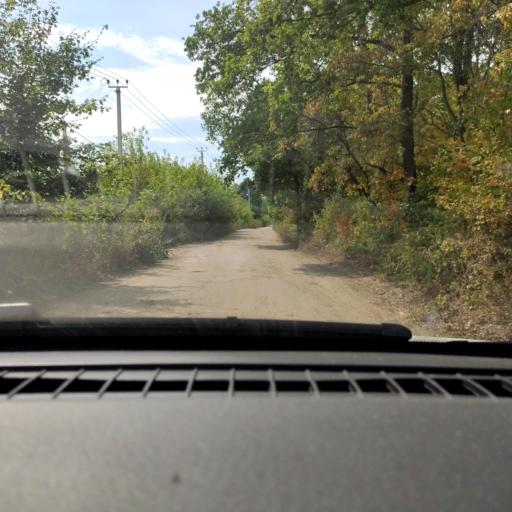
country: RU
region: Voronezj
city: Pridonskoy
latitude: 51.7536
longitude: 39.0788
